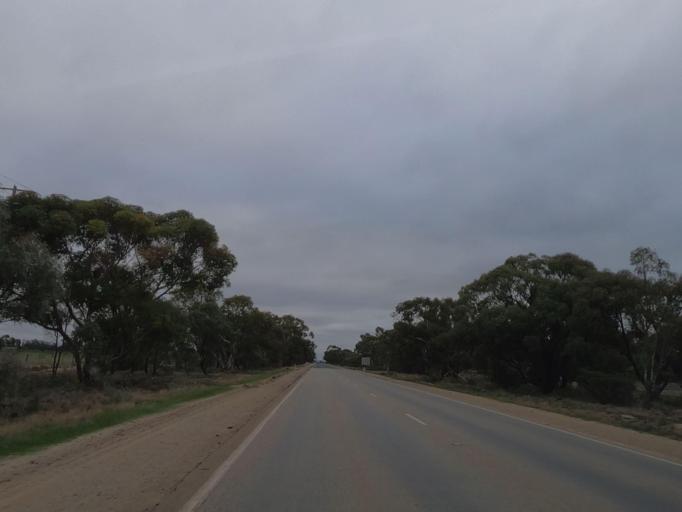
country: AU
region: Victoria
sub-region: Swan Hill
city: Swan Hill
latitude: -35.4022
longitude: 143.5784
